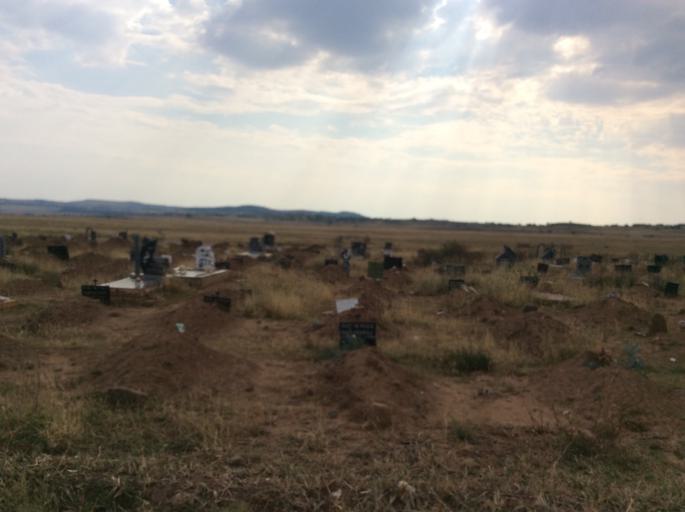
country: LS
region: Mafeteng
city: Mafeteng
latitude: -29.7088
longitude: 27.0135
